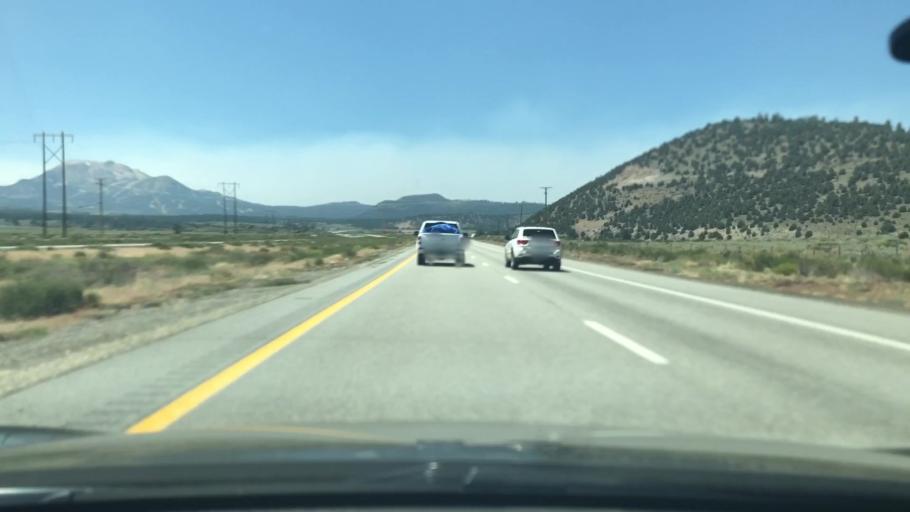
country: US
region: California
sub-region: Mono County
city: Mammoth Lakes
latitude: 37.6347
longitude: -118.8819
